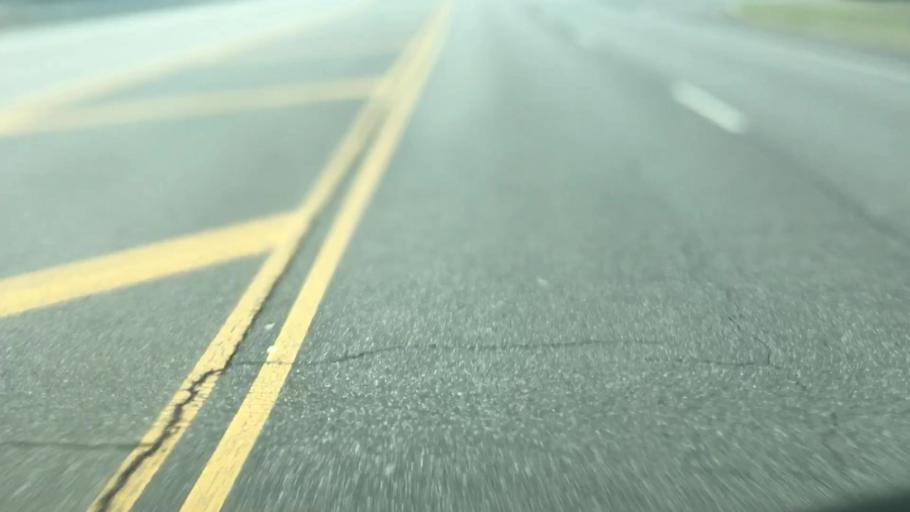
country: US
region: Alabama
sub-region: Walker County
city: Jasper
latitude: 33.8177
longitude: -87.2335
